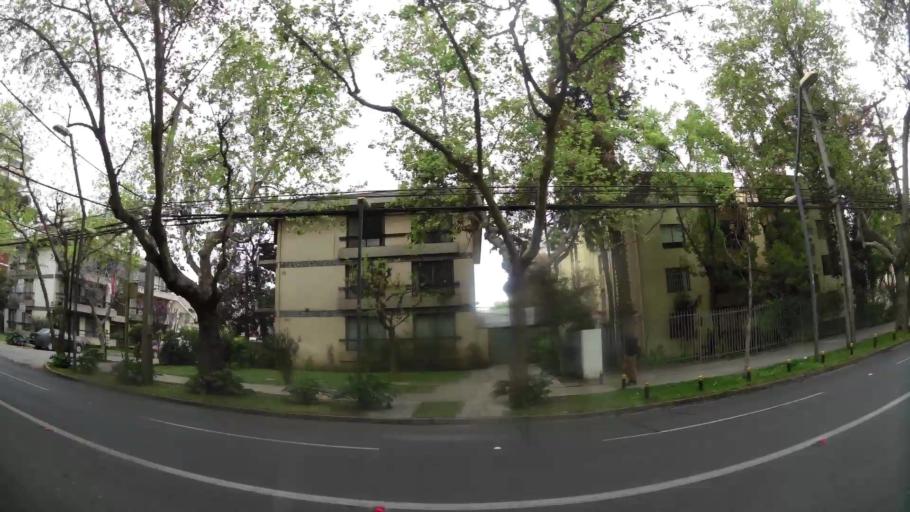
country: CL
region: Santiago Metropolitan
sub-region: Provincia de Santiago
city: Villa Presidente Frei, Nunoa, Santiago, Chile
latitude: -33.4247
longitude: -70.5841
